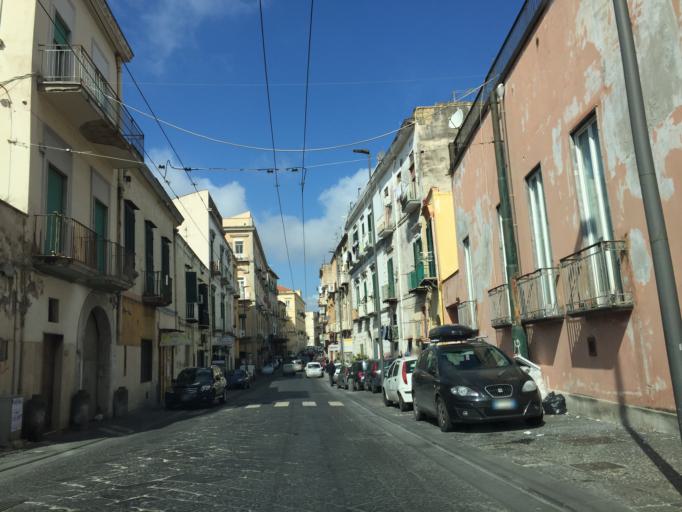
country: IT
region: Campania
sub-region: Provincia di Napoli
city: Ercolano
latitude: 40.8039
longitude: 14.3512
